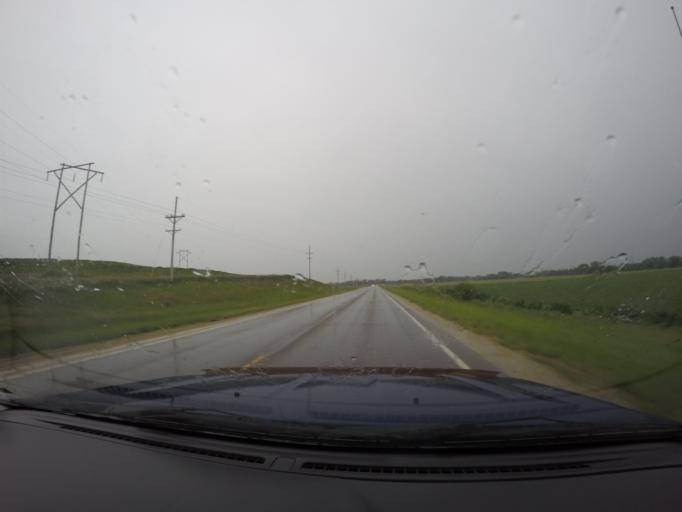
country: US
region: Kansas
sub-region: Cloud County
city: Concordia
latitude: 39.5738
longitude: -97.6975
